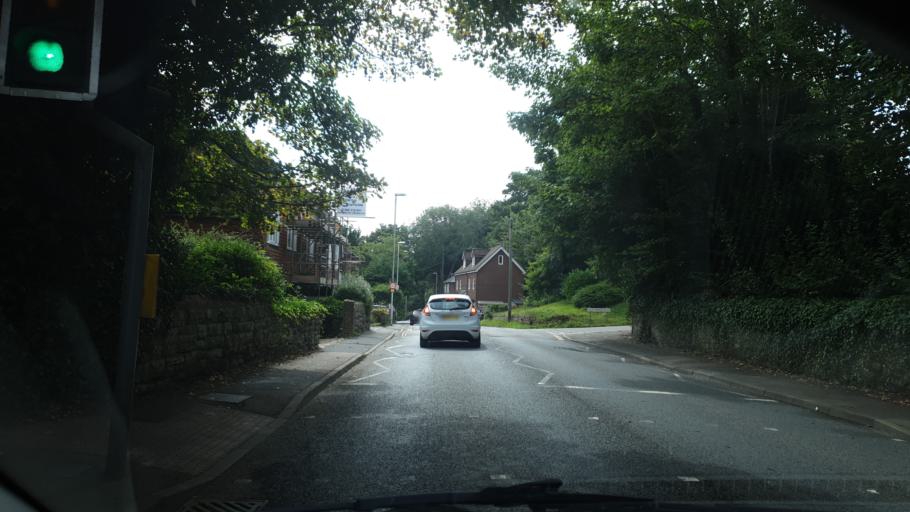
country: GB
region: England
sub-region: West Sussex
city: East Grinstead
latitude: 51.1262
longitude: -0.0036
